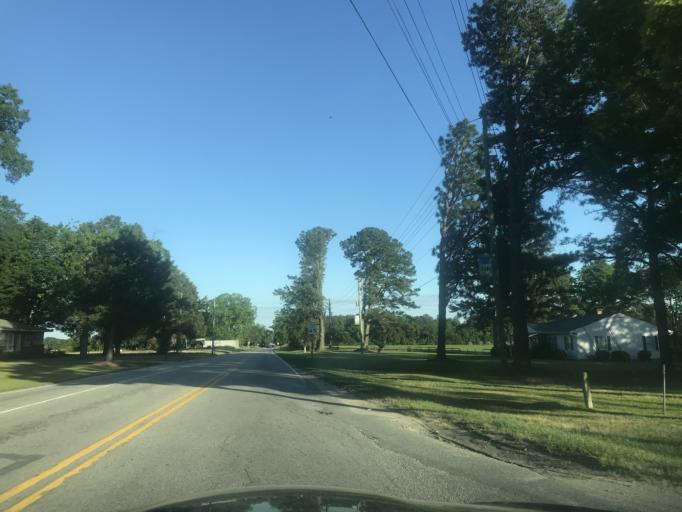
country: US
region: North Carolina
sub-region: Johnston County
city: Archer Lodge
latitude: 35.6920
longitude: -78.3728
